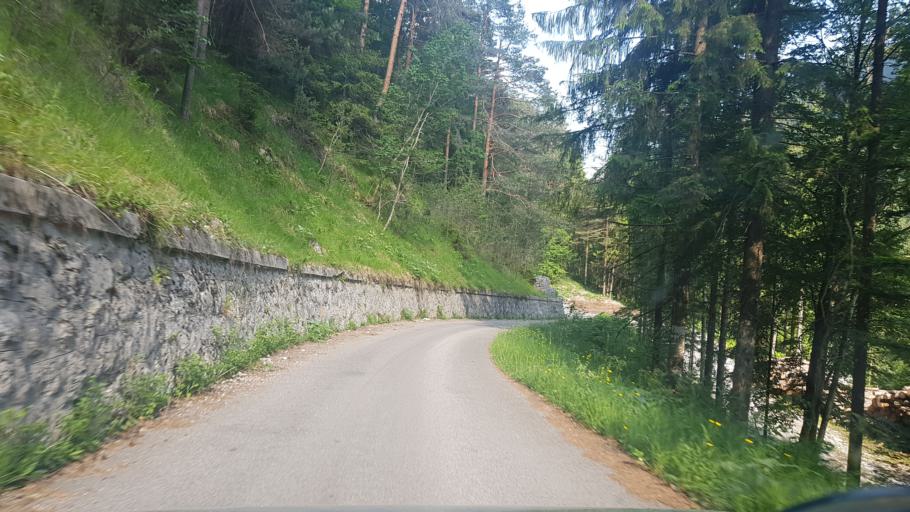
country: IT
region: Friuli Venezia Giulia
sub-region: Provincia di Udine
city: Pontebba
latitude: 46.5264
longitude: 13.2239
